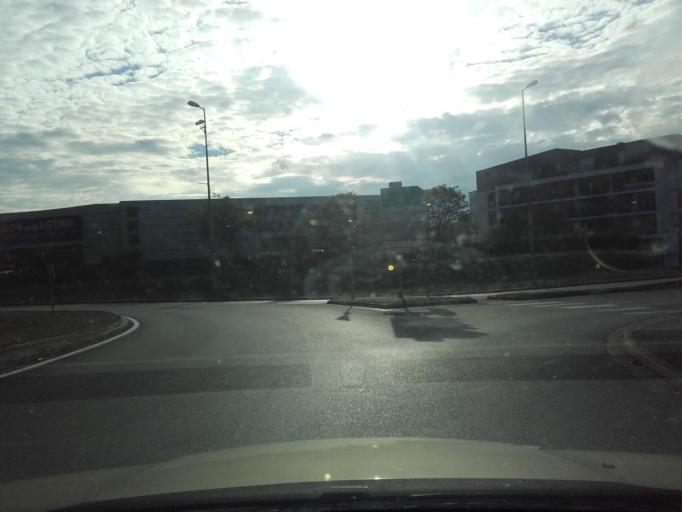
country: FR
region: Centre
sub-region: Departement d'Indre-et-Loire
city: Chanceaux-sur-Choisille
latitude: 47.4306
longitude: 0.7048
